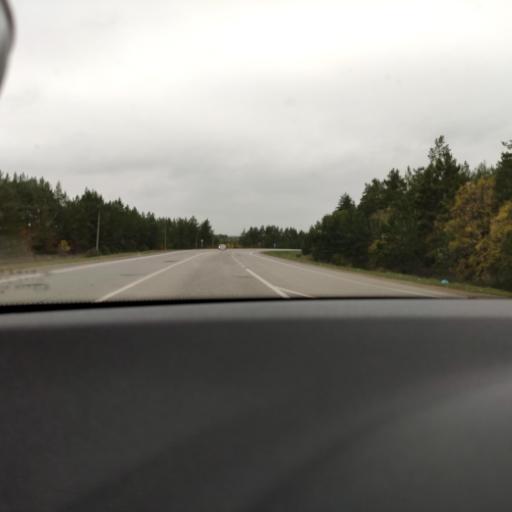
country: RU
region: Samara
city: Mirnyy
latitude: 53.5288
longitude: 50.3078
